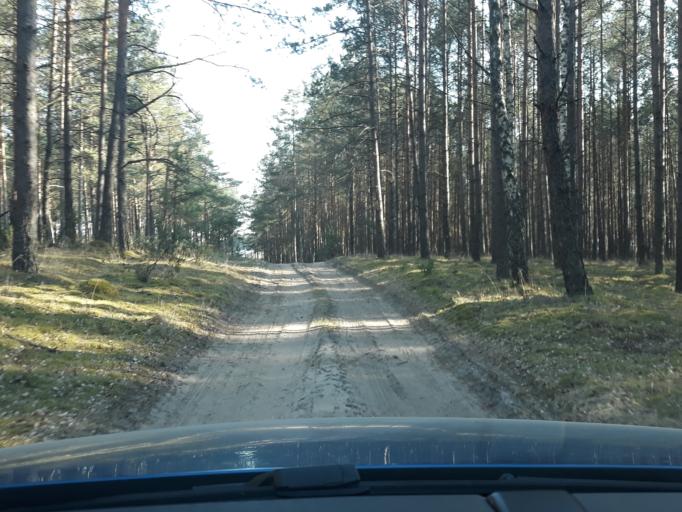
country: PL
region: Pomeranian Voivodeship
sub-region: Powiat bytowski
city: Lipnica
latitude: 53.8961
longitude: 17.4940
